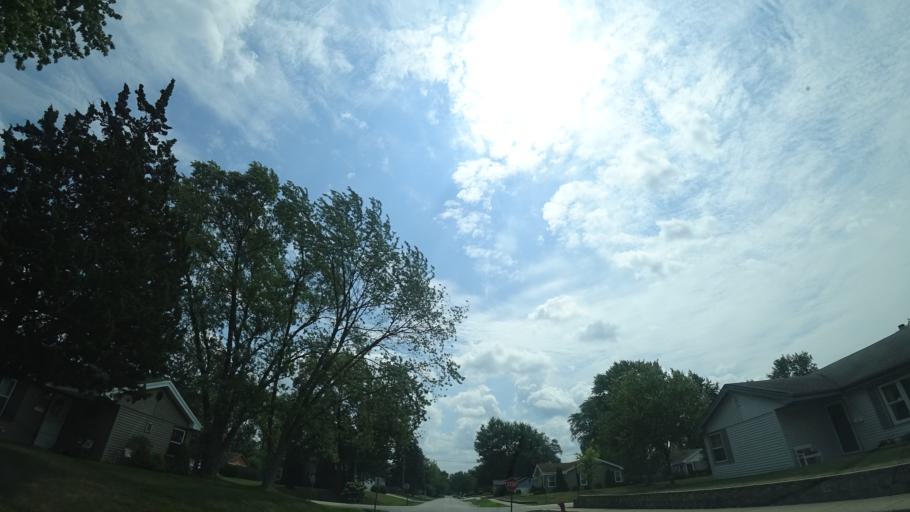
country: US
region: Illinois
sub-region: Cook County
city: Worth
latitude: 41.6868
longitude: -87.7914
